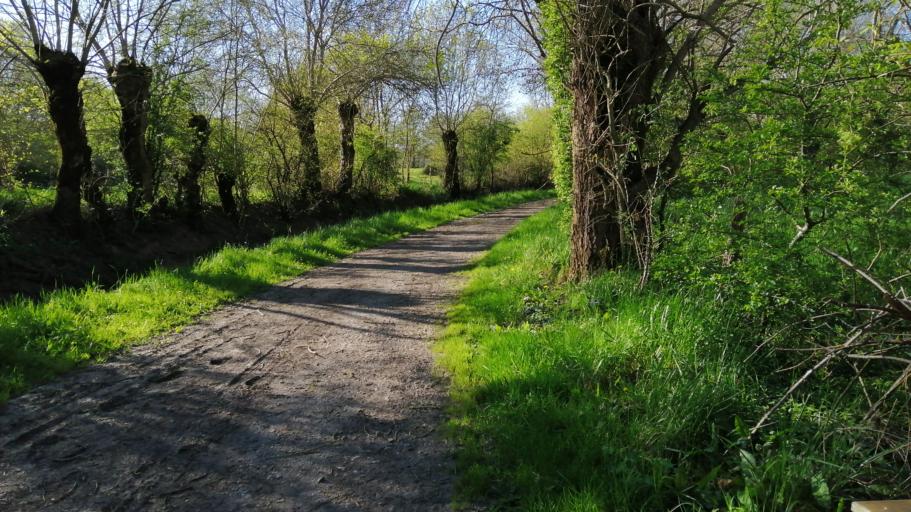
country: FR
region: Pays de la Loire
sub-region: Departement de la Loire-Atlantique
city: Saint-Gereon
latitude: 47.3575
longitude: -1.2013
